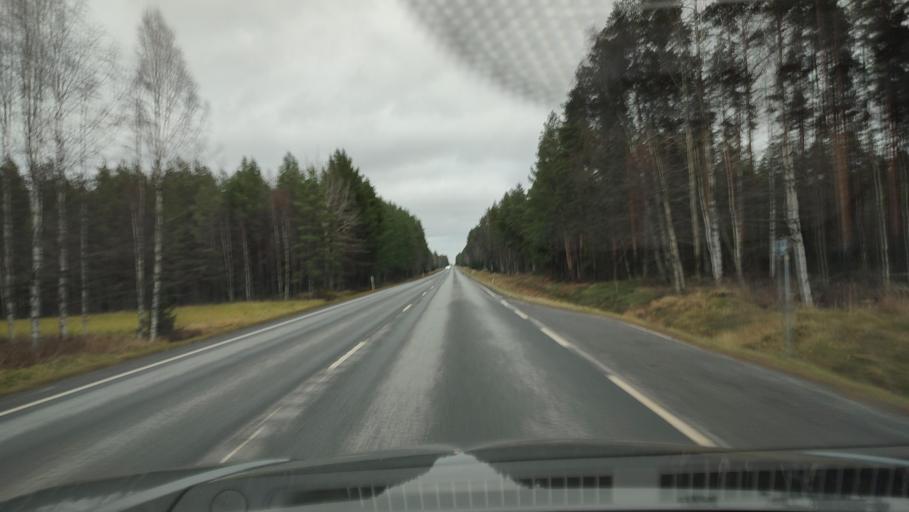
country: FI
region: Southern Ostrobothnia
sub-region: Seinaejoki
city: Kurikka
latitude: 62.5205
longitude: 22.3180
